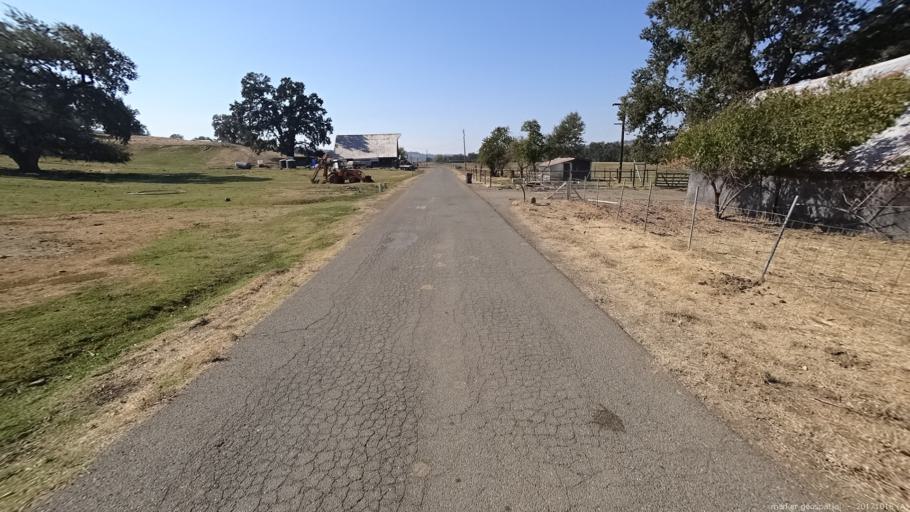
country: US
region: California
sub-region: Shasta County
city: Shingletown
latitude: 40.5547
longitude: -122.0556
